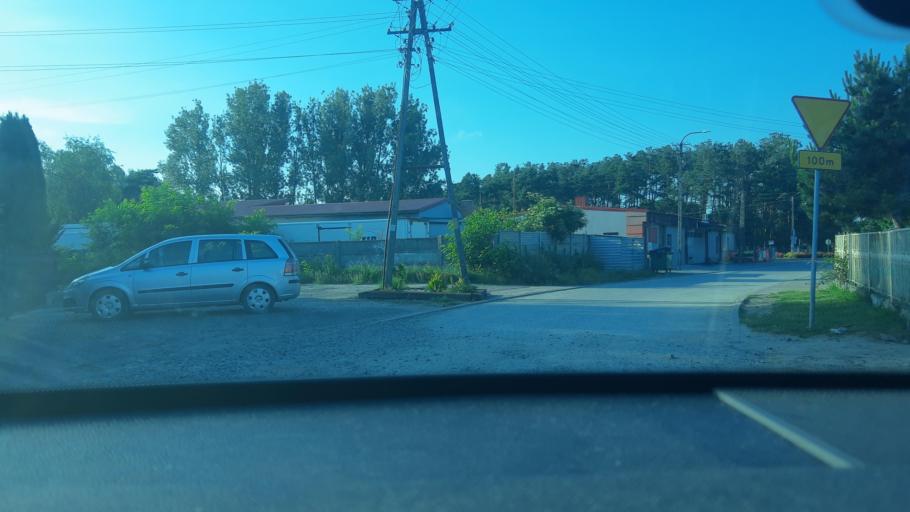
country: PL
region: Lodz Voivodeship
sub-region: Powiat sieradzki
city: Burzenin
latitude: 51.4574
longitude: 18.8414
